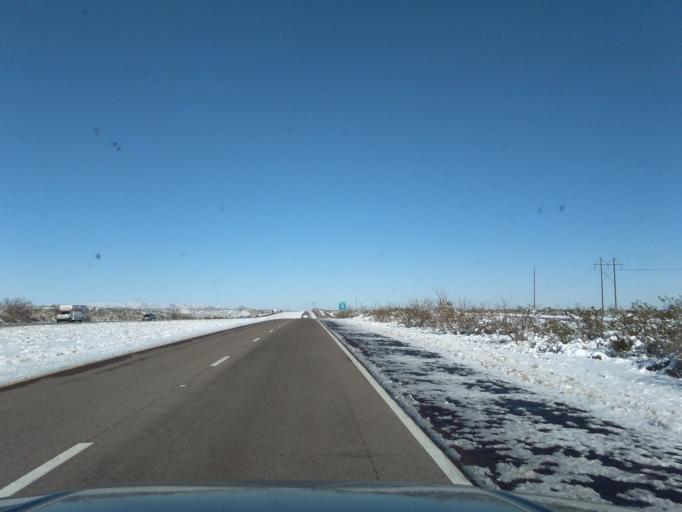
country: US
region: New Mexico
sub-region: Socorro County
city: Socorro
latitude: 33.6417
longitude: -107.1150
